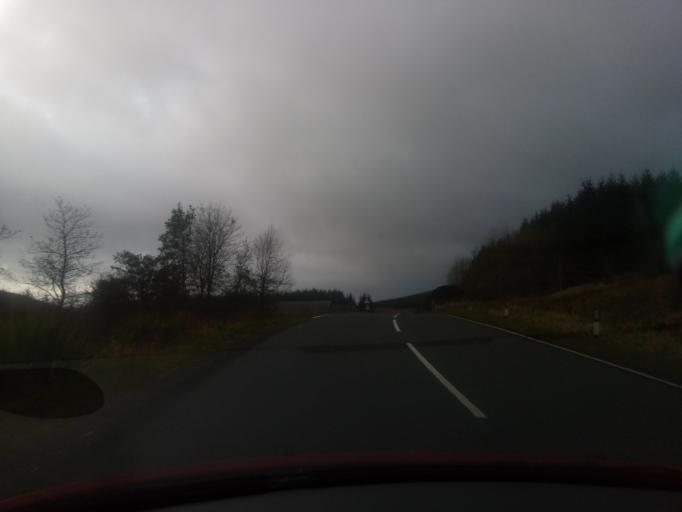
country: GB
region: Scotland
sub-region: The Scottish Borders
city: Hawick
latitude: 55.3087
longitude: -2.6564
